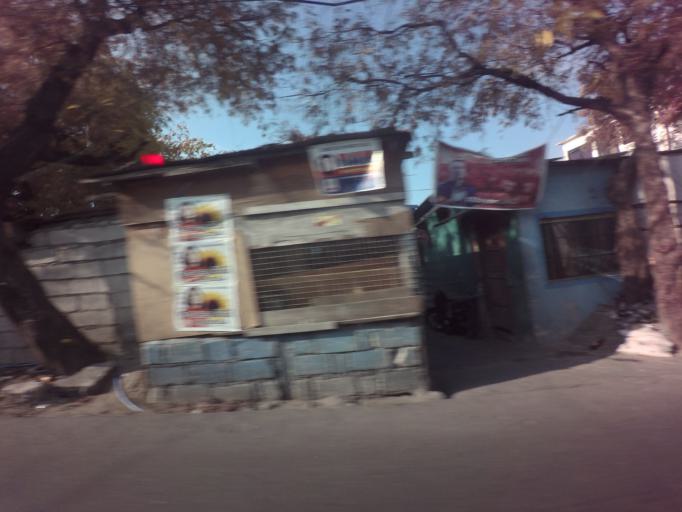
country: PH
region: Calabarzon
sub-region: Province of Rizal
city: Taguig
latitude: 14.4802
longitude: 121.0587
